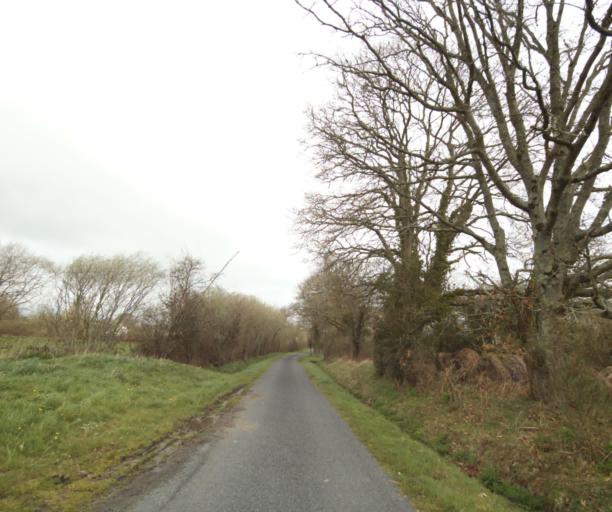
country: FR
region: Pays de la Loire
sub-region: Departement de la Loire-Atlantique
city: Bouvron
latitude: 47.4229
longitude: -1.8934
